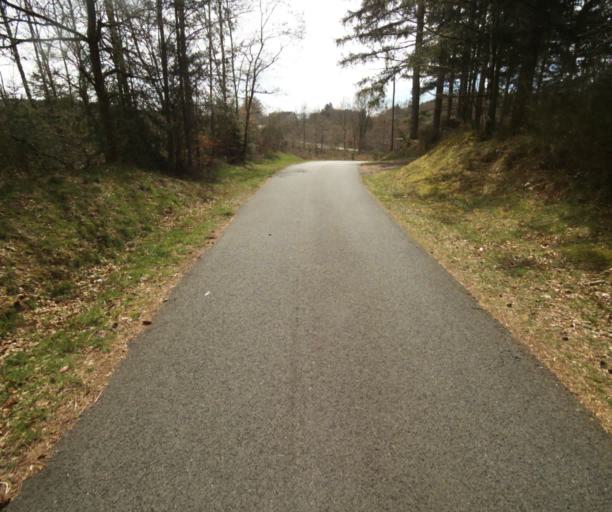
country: FR
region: Limousin
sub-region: Departement de la Correze
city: Egletons
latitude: 45.3701
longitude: 1.9689
